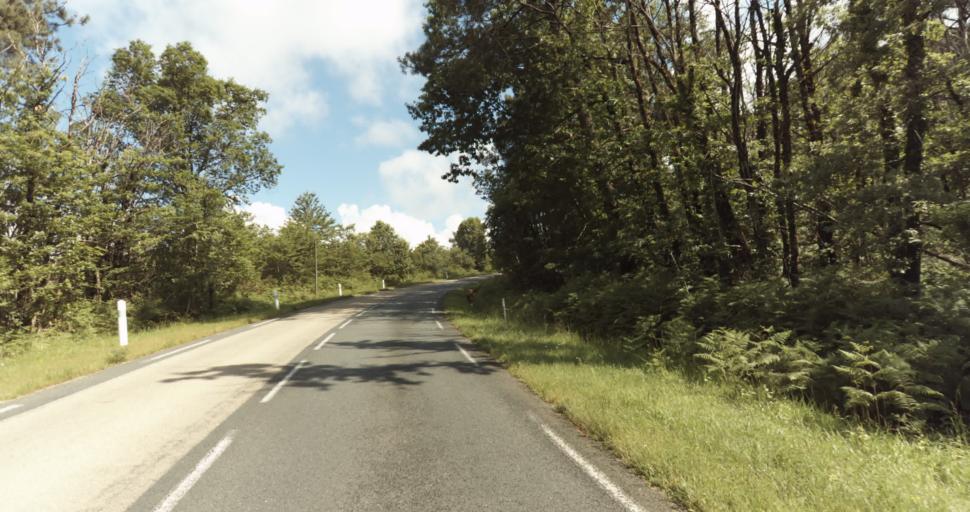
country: FR
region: Aquitaine
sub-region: Departement de la Dordogne
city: Le Bugue
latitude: 44.8408
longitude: 0.8698
